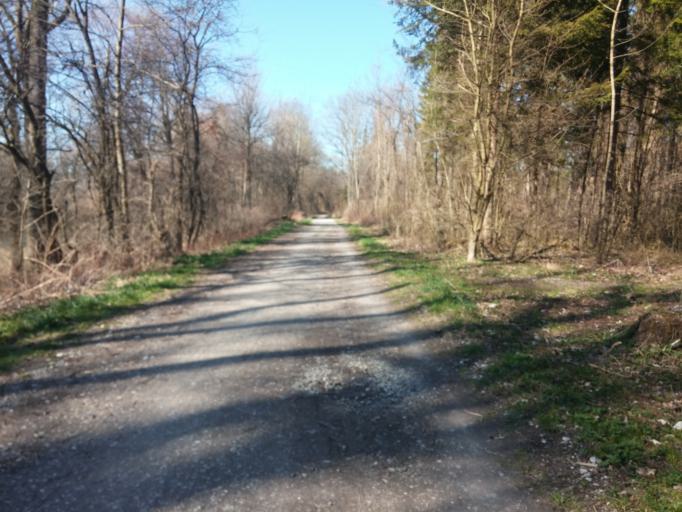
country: DE
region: Bavaria
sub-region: Upper Bavaria
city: Ismaning
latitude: 48.2392
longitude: 11.6741
